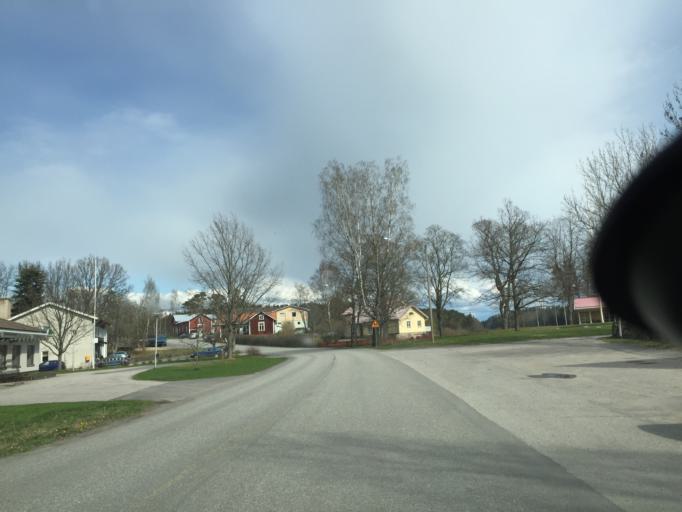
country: FI
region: Varsinais-Suomi
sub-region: Salo
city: Saerkisalo
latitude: 59.9885
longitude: 23.0320
